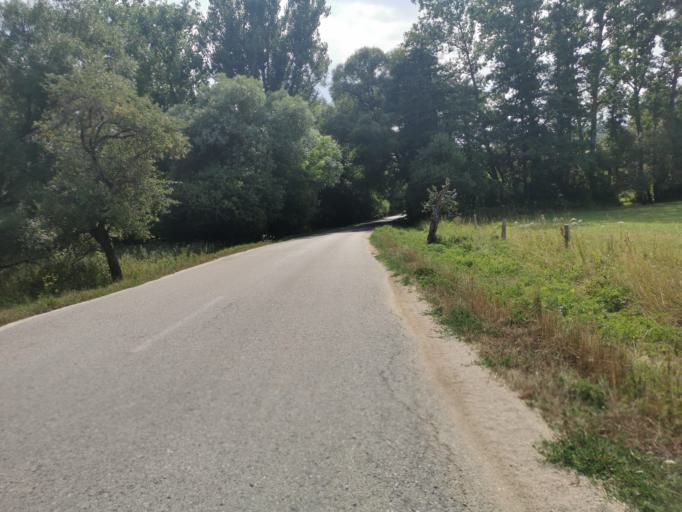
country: SK
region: Trenciansky
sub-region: Okres Myjava
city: Myjava
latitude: 48.7425
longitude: 17.5177
